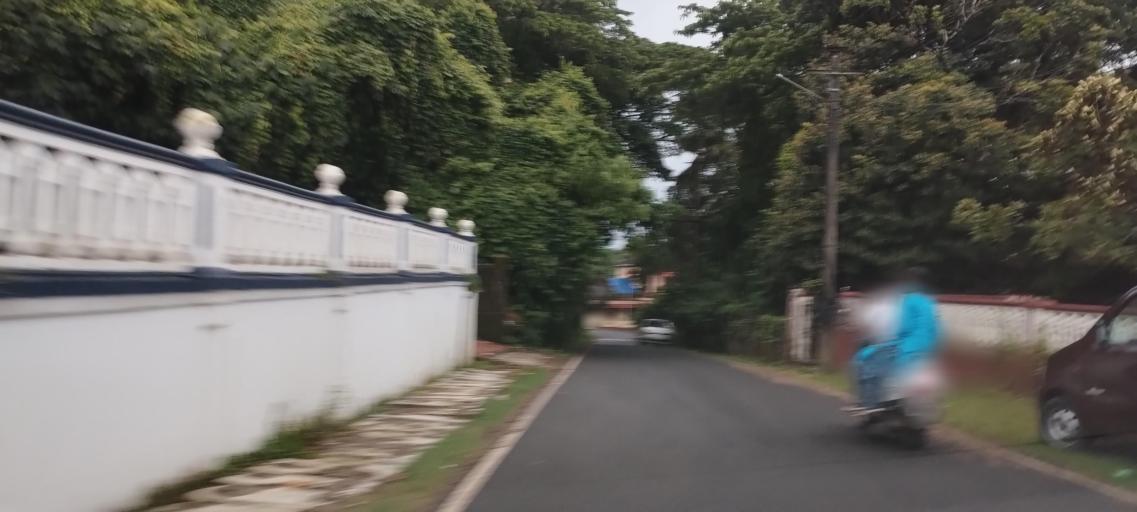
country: IN
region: Goa
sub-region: North Goa
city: Jua
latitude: 15.5261
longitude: 73.9028
